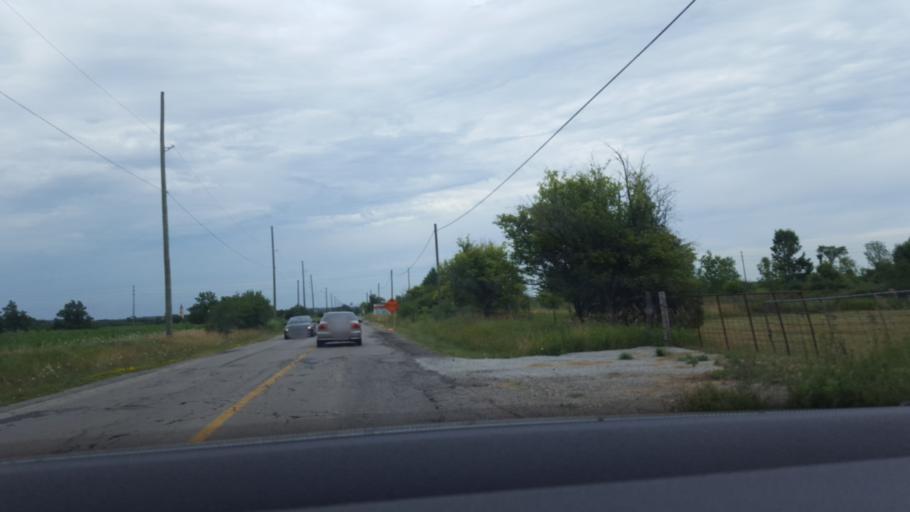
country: CA
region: Ontario
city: Brampton
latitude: 43.6161
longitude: -79.8375
